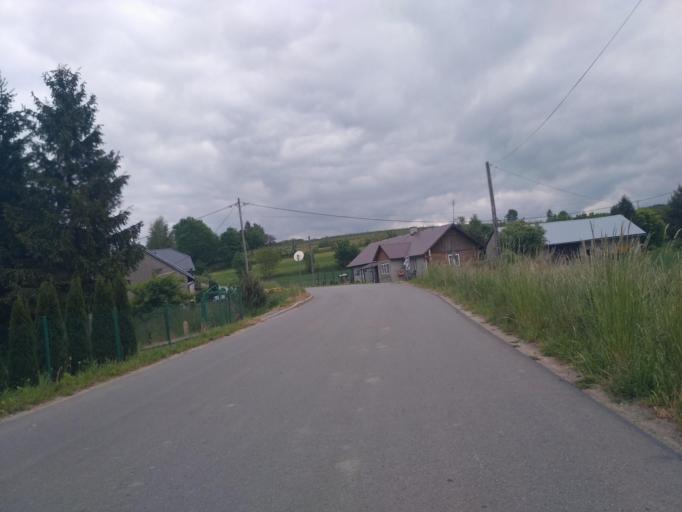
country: PL
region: Subcarpathian Voivodeship
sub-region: Powiat jasielski
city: Tarnowiec
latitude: 49.7130
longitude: 21.5886
